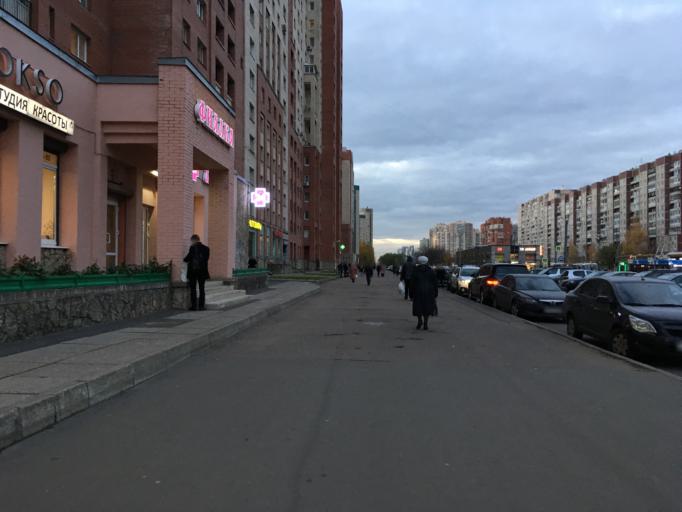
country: RU
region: St.-Petersburg
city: Staraya Derevnya
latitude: 60.0204
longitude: 30.2437
